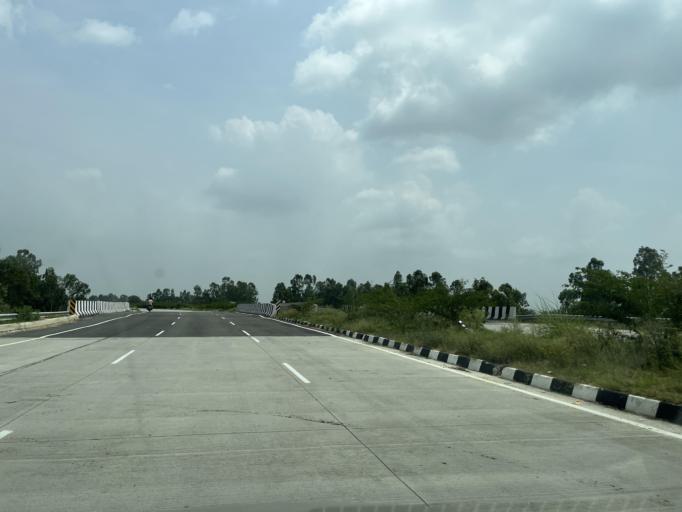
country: IN
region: Uttar Pradesh
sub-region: Bijnor
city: Nagina
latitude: 29.4315
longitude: 78.4051
